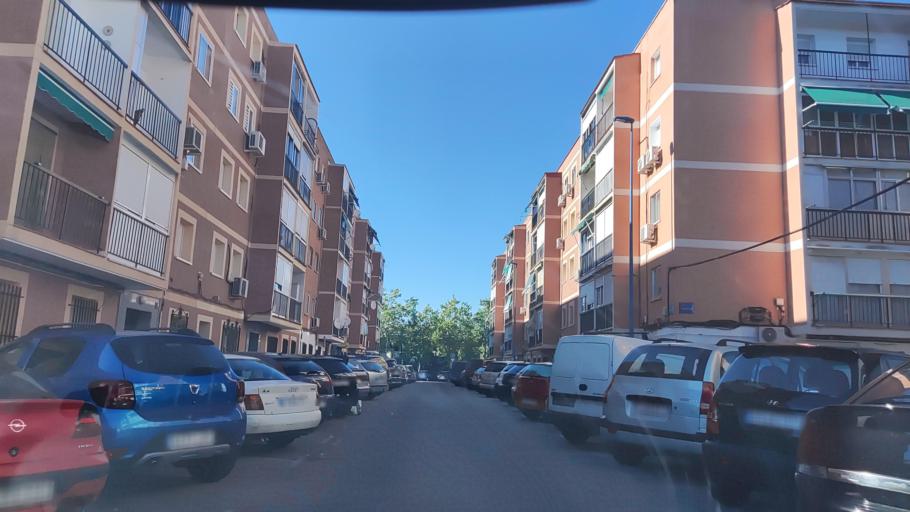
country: ES
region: Madrid
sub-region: Provincia de Madrid
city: Leganes
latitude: 40.3354
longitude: -3.7682
